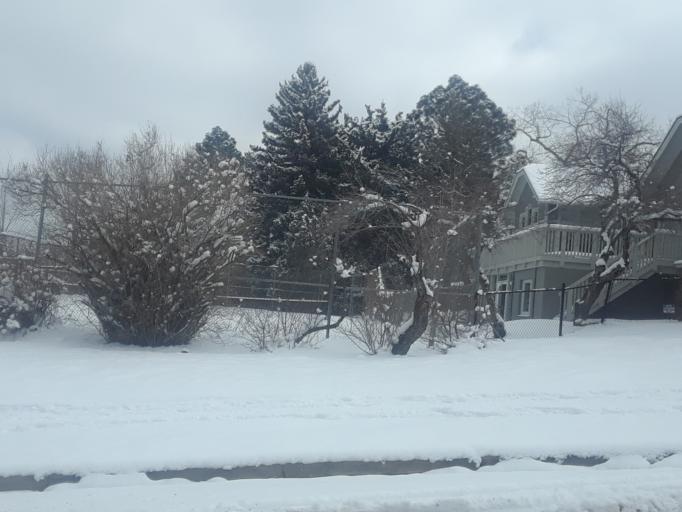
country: US
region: Colorado
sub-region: Boulder County
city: Boulder
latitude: 40.0005
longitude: -105.2867
